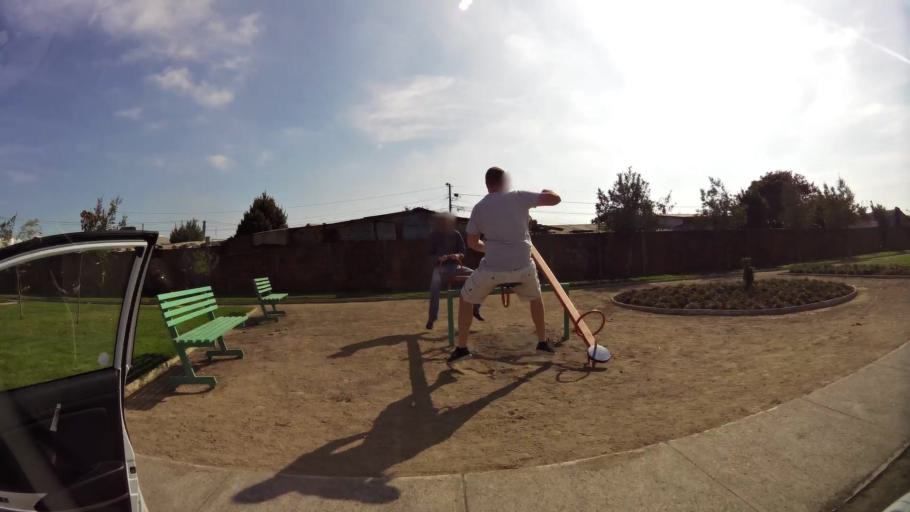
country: CL
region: Biobio
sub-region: Provincia de Concepcion
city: Talcahuano
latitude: -36.7871
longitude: -73.1164
